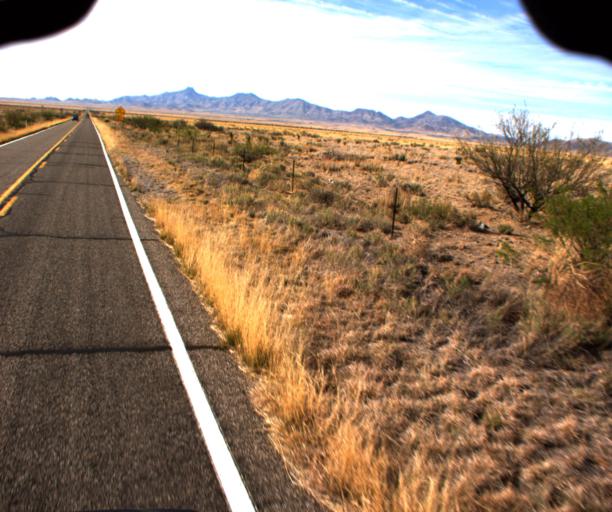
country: US
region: Arizona
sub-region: Cochise County
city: Willcox
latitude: 32.0365
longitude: -109.4774
